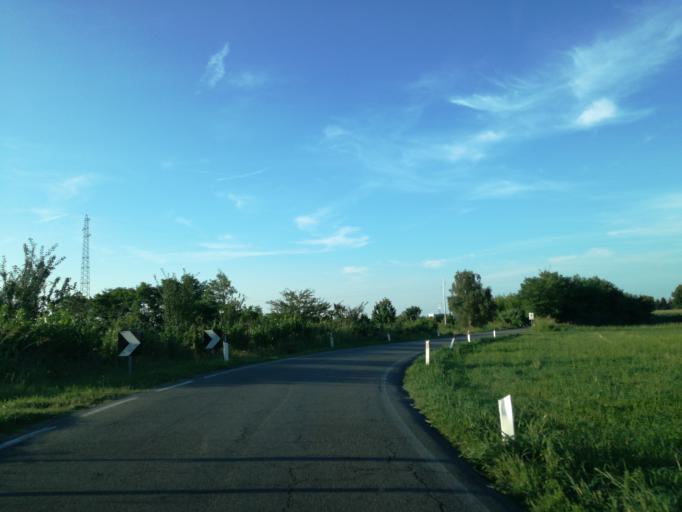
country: IT
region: Lombardy
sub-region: Provincia di Monza e Brianza
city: Sulbiate
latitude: 45.6517
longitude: 9.4306
